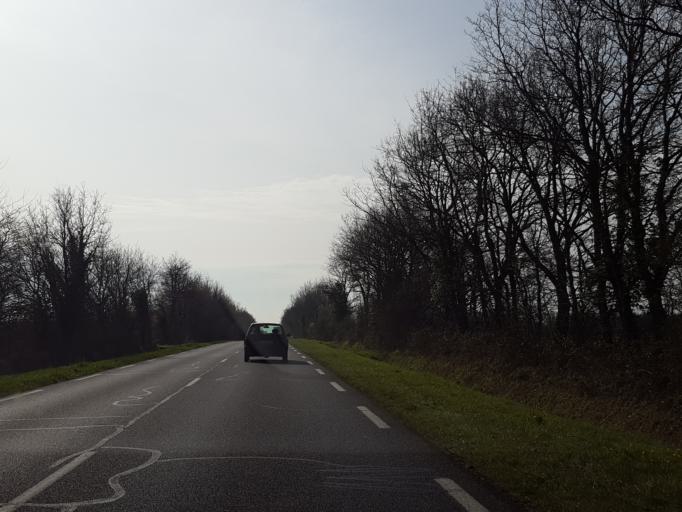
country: FR
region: Pays de la Loire
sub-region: Departement de la Vendee
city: Saligny
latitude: 46.8102
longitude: -1.4592
